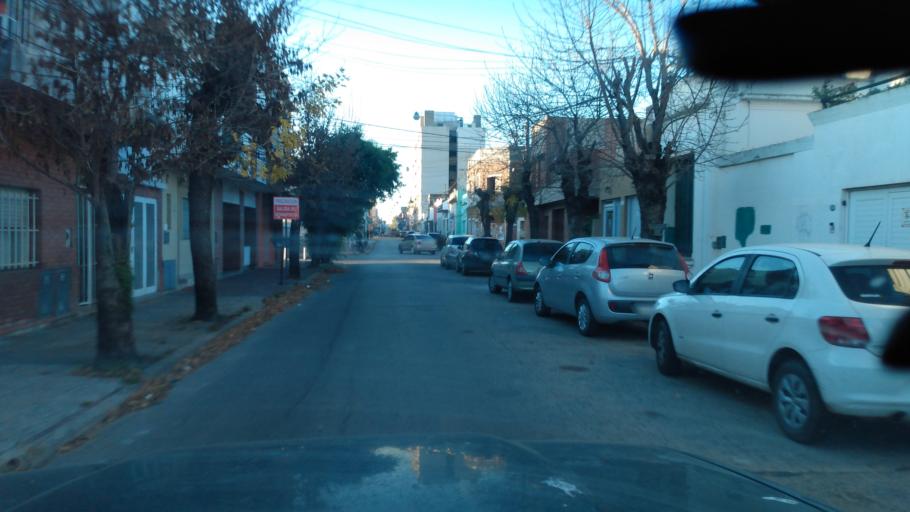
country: AR
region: Buenos Aires
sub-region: Partido de Lujan
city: Lujan
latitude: -34.5675
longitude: -59.1191
